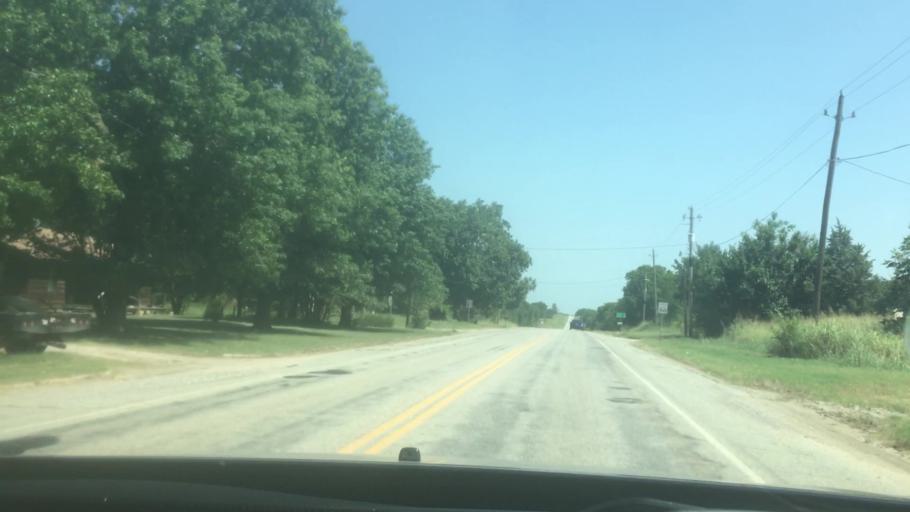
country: US
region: Oklahoma
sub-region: Coal County
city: Coalgate
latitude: 34.3773
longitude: -96.4245
